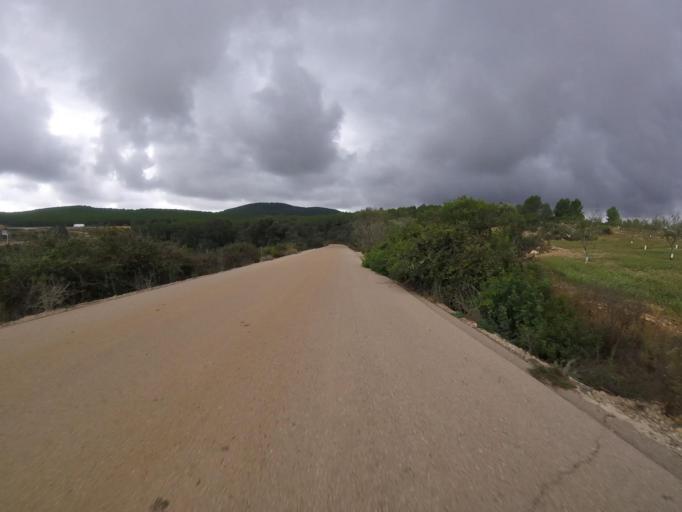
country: ES
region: Valencia
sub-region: Provincia de Castello
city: Benlloch
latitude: 40.2021
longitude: 0.0657
